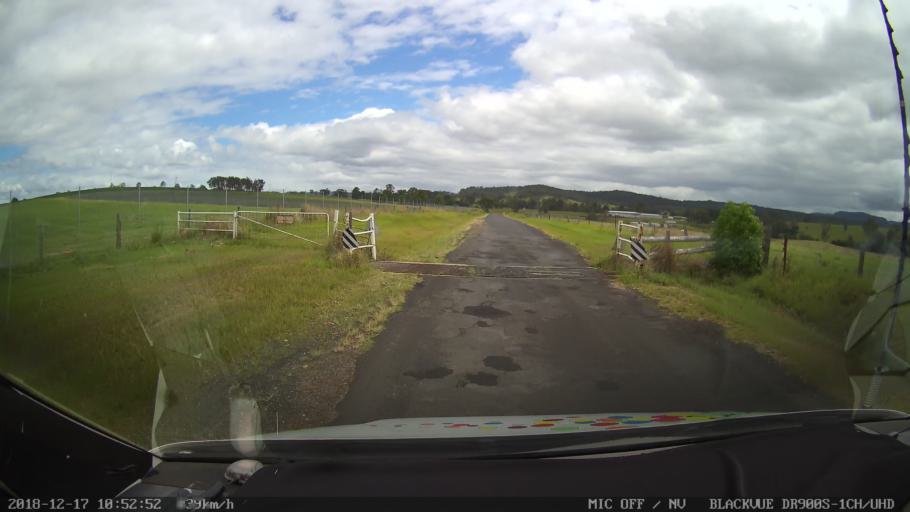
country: AU
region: New South Wales
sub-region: Tenterfield Municipality
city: Carrolls Creek
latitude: -28.8418
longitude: 152.5626
